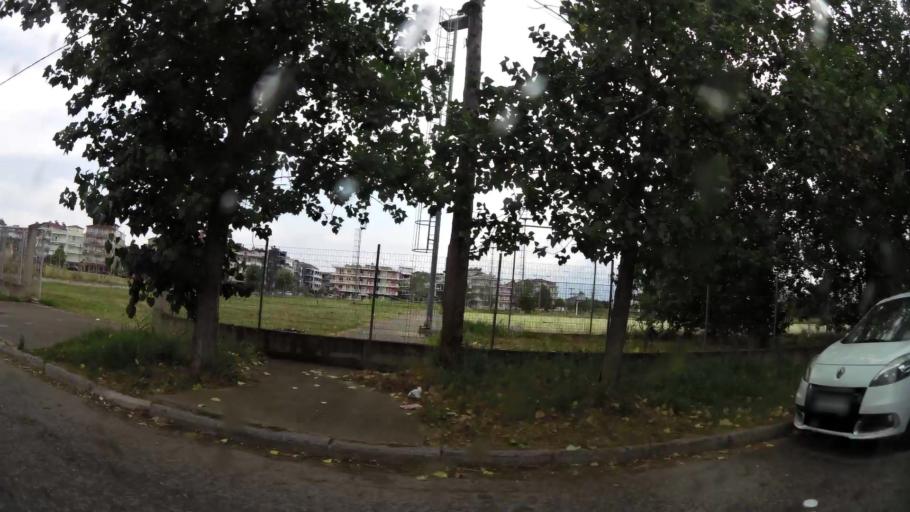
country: GR
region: Central Macedonia
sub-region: Nomos Pierias
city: Paralia
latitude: 40.2717
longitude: 22.5955
